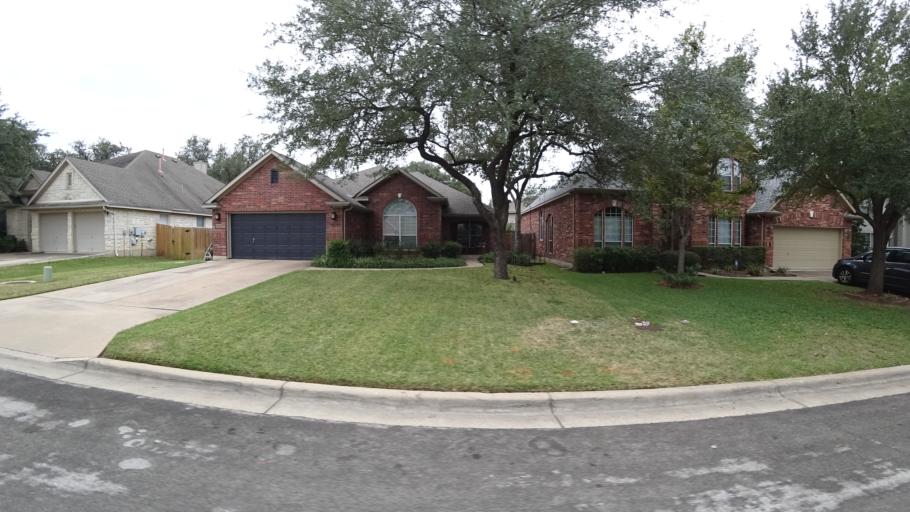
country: US
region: Texas
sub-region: Travis County
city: Shady Hollow
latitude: 30.2073
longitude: -97.8812
